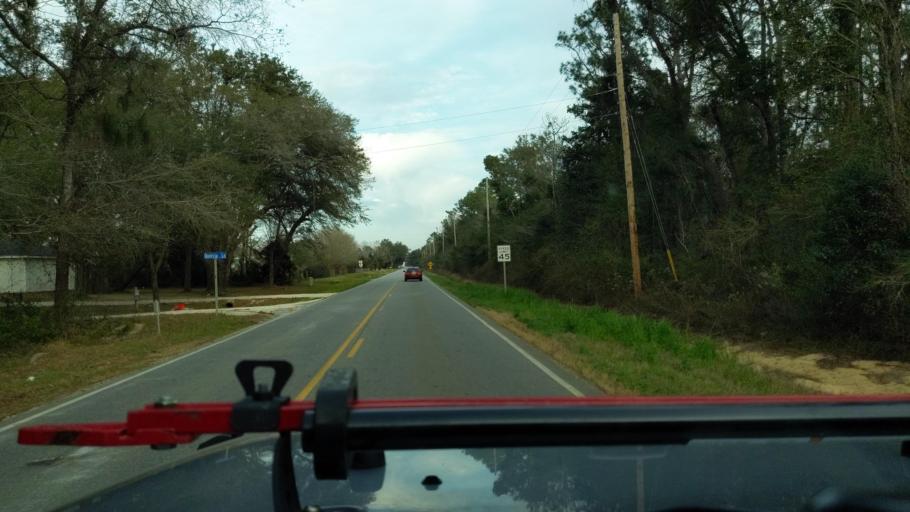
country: US
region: Alabama
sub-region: Baldwin County
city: Foley
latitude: 30.4579
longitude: -87.7750
